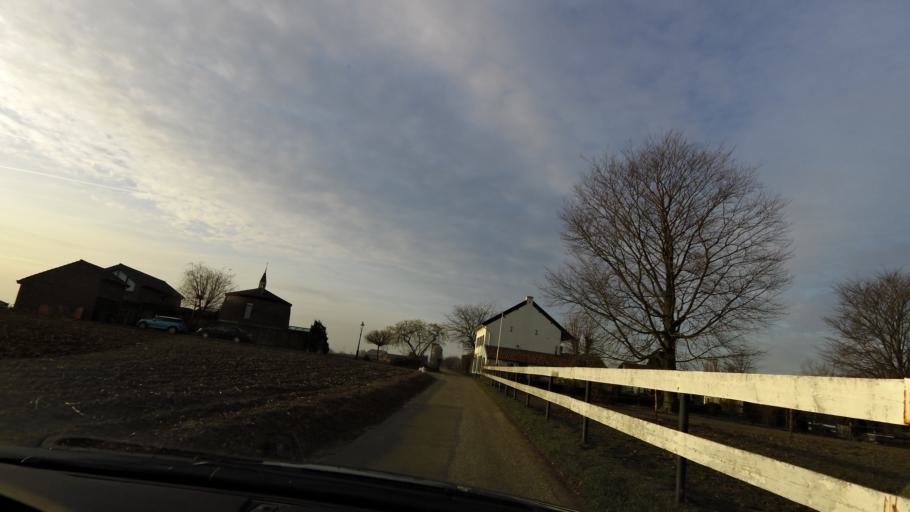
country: NL
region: Limburg
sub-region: Valkenburg aan de Geul
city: Broekhem
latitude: 50.9039
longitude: 5.8290
